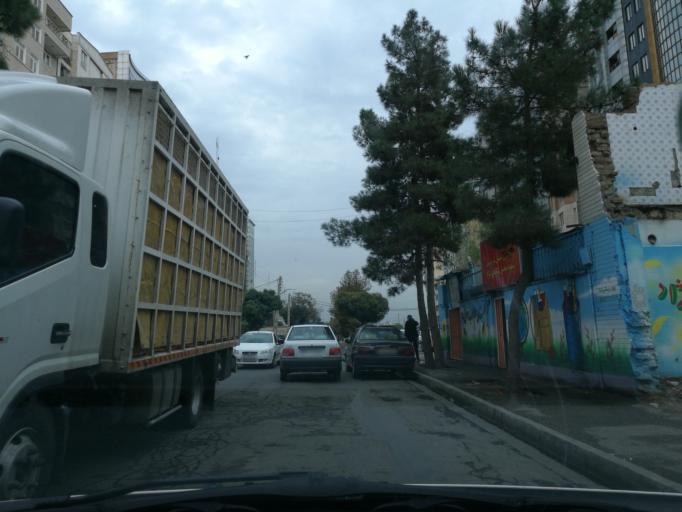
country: IR
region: Alborz
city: Karaj
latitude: 35.8551
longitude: 50.9558
